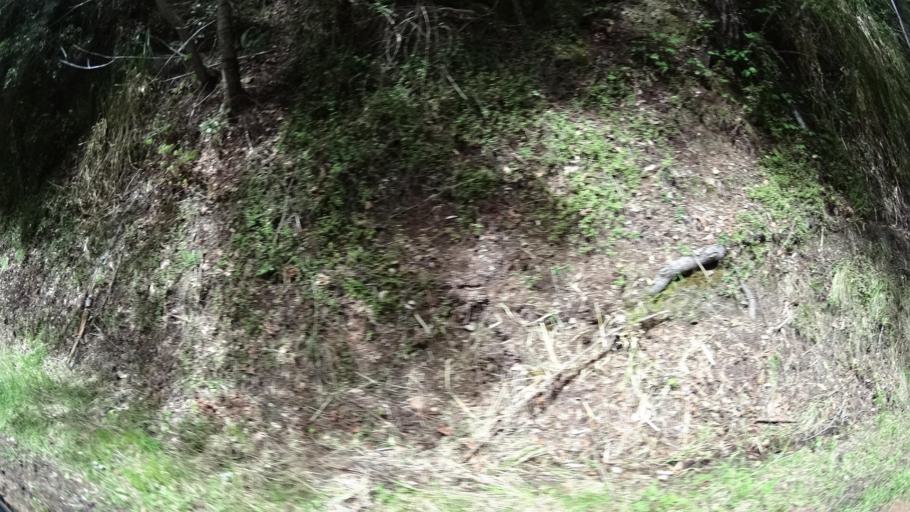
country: US
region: California
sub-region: Humboldt County
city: Blue Lake
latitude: 40.7601
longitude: -123.9191
